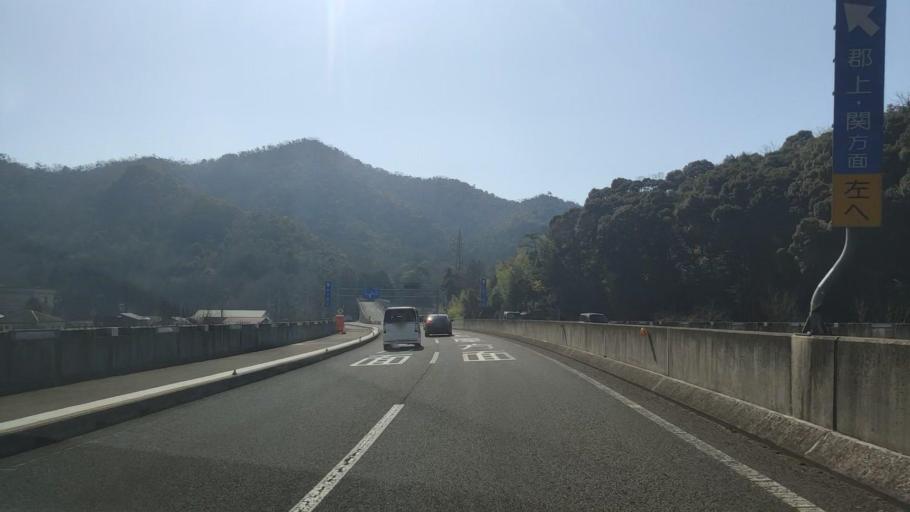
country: JP
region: Gifu
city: Gifu-shi
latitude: 35.4303
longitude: 136.7957
